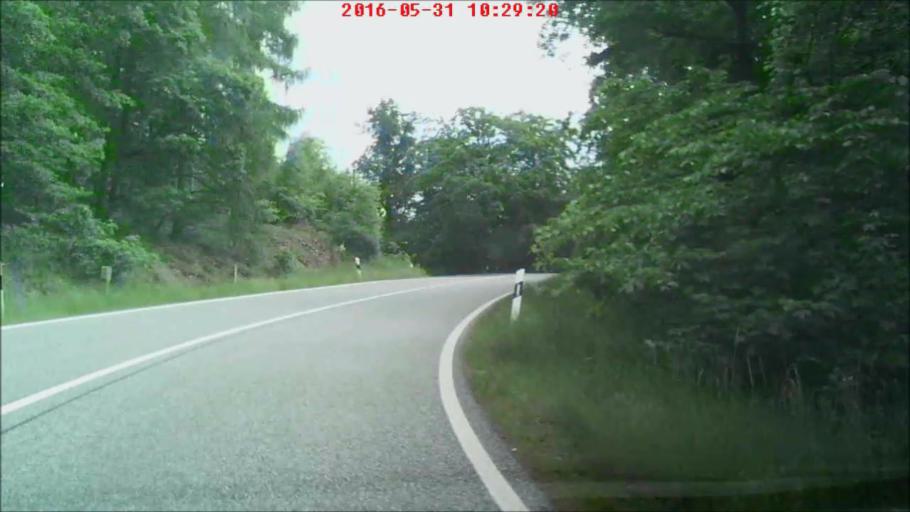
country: DE
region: Saxony-Anhalt
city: Kelbra
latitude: 51.4157
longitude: 11.0772
